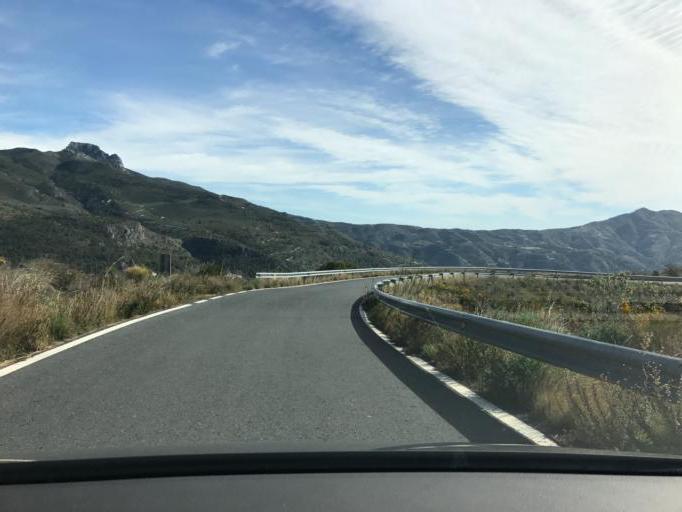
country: ES
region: Andalusia
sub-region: Provincia de Granada
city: Otivar
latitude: 36.8219
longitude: -3.6958
